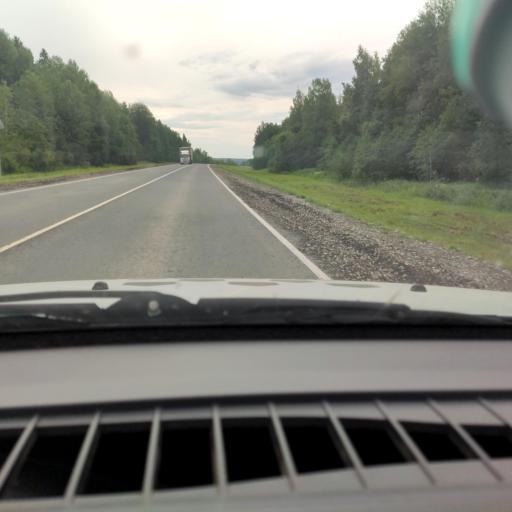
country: RU
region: Kirov
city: Kostino
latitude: 58.8144
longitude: 53.5877
